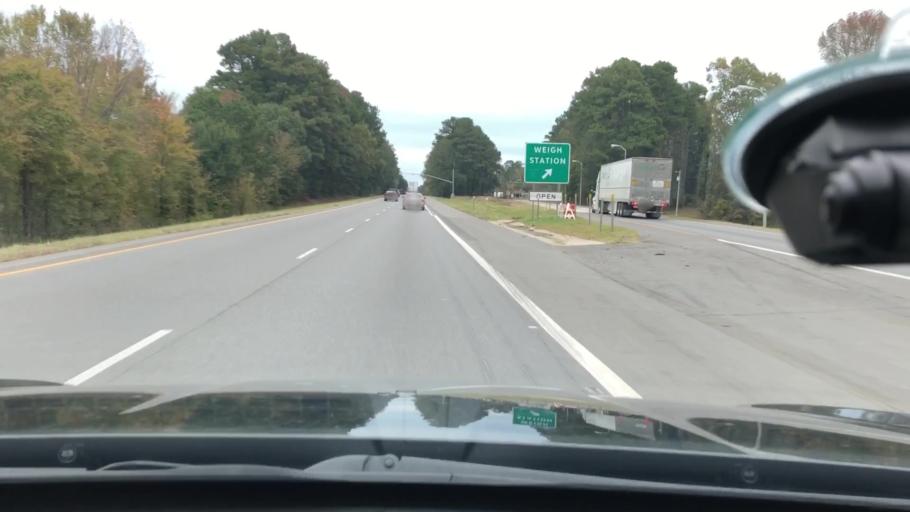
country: US
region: Arkansas
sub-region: Hempstead County
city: Hope
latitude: 33.6485
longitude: -93.6756
